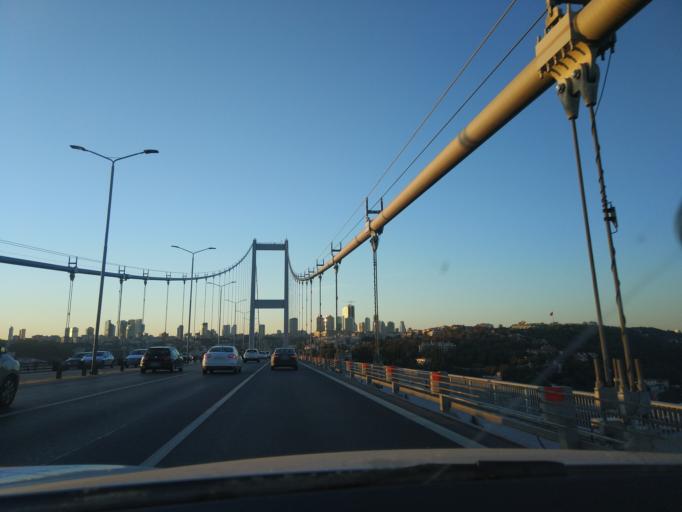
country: TR
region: Istanbul
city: UEskuedar
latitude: 41.0463
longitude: 29.0337
